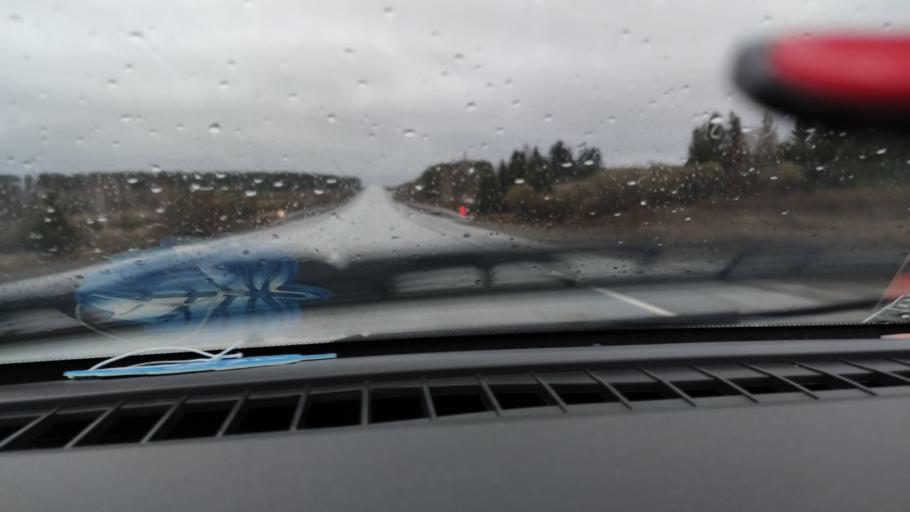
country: RU
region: Udmurtiya
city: Alnashi
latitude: 56.0567
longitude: 52.3931
